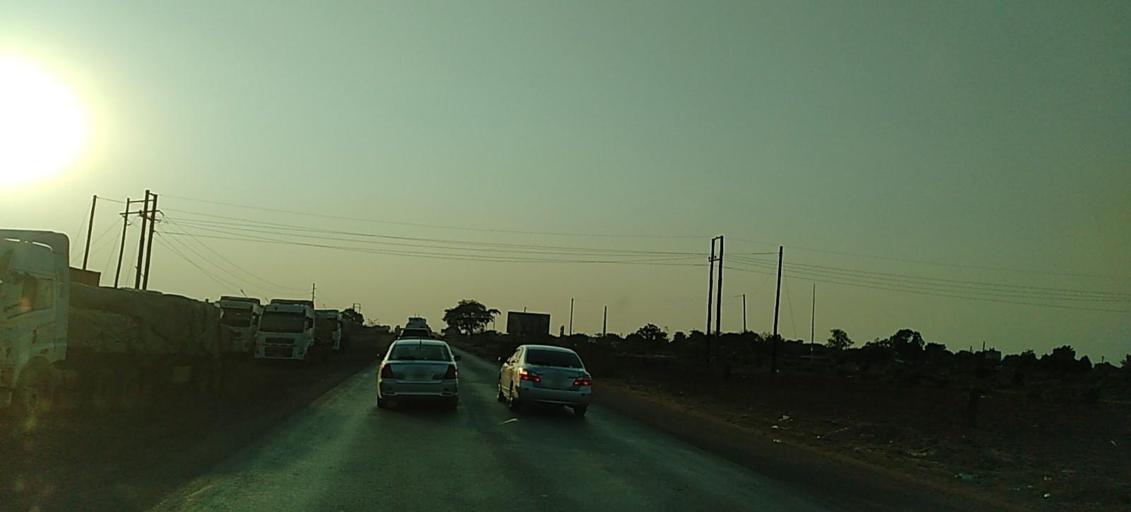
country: ZM
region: Copperbelt
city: Ndola
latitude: -13.0292
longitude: 28.6823
